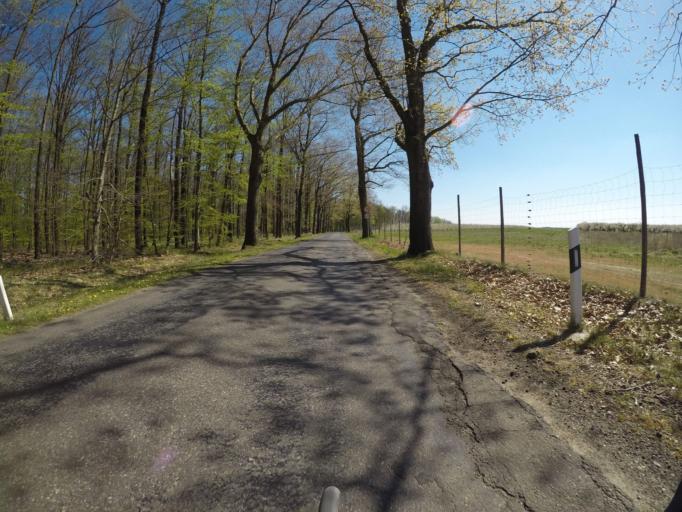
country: DE
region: Brandenburg
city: Werftpfuhl
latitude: 52.6241
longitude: 13.8211
